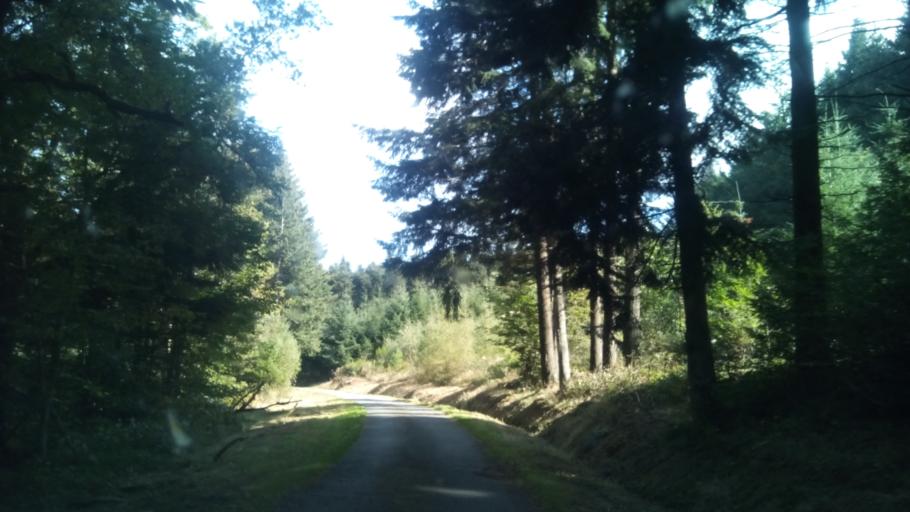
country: FR
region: Rhone-Alpes
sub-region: Departement du Rhone
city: Beaujeu
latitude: 46.2051
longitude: 4.5177
